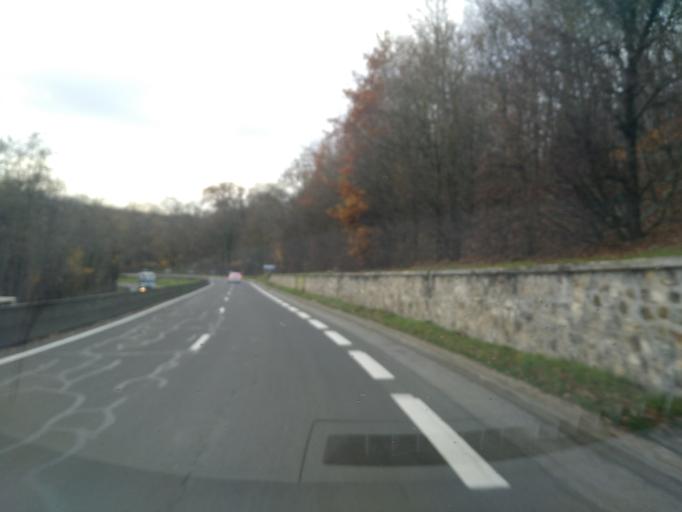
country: FR
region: Ile-de-France
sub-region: Departement des Yvelines
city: Guyancourt
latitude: 48.7814
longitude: 2.0982
